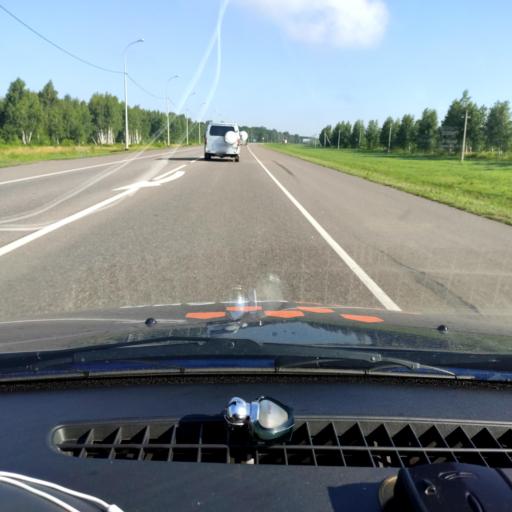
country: RU
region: Orjol
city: Orel
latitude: 52.8913
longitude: 36.1593
